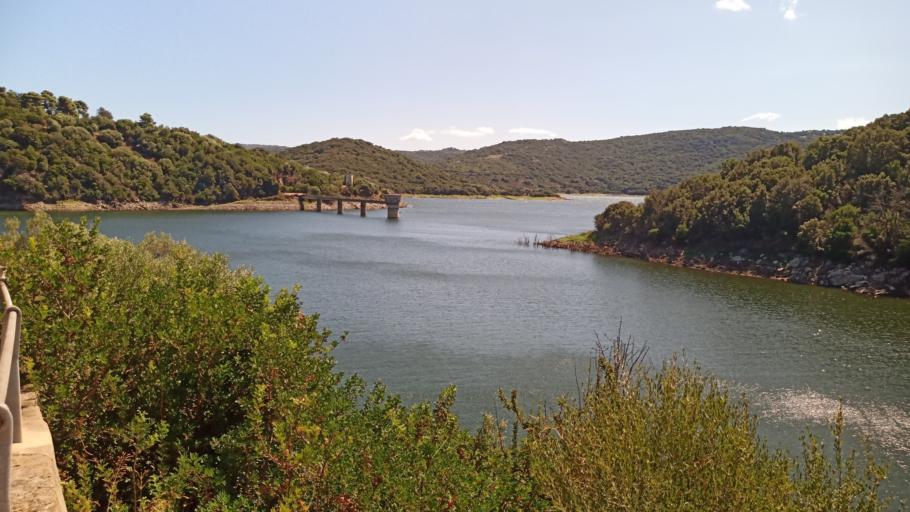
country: IT
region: Sardinia
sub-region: Provincia di Olbia-Tempio
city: Sant'Antonio di Gallura
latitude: 41.0148
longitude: 9.2718
